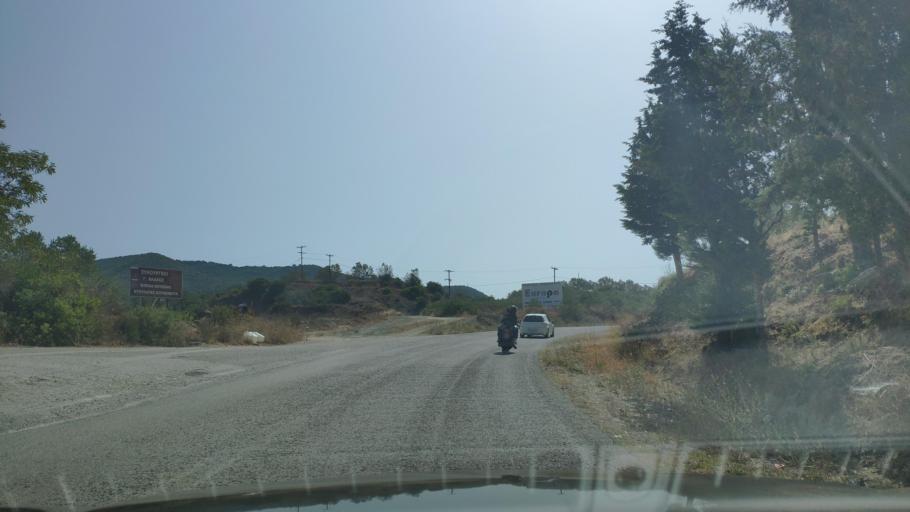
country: GR
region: Epirus
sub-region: Nomos Artas
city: Peta
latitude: 39.1686
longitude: 21.0490
